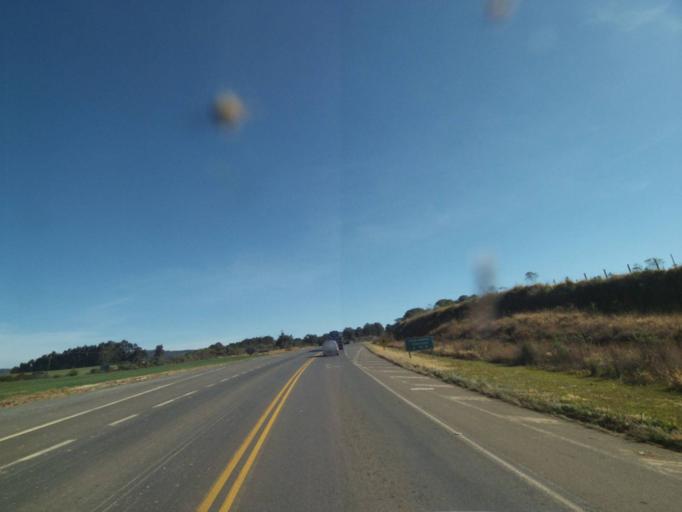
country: BR
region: Parana
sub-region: Tibagi
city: Tibagi
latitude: -24.5259
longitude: -50.4439
